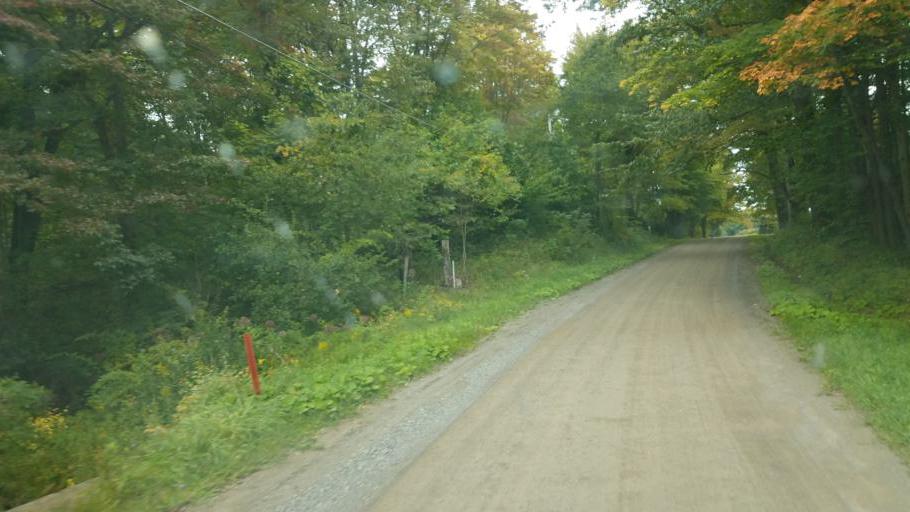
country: US
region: Pennsylvania
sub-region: Crawford County
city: Pymatuning Central
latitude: 41.5403
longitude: -80.4578
